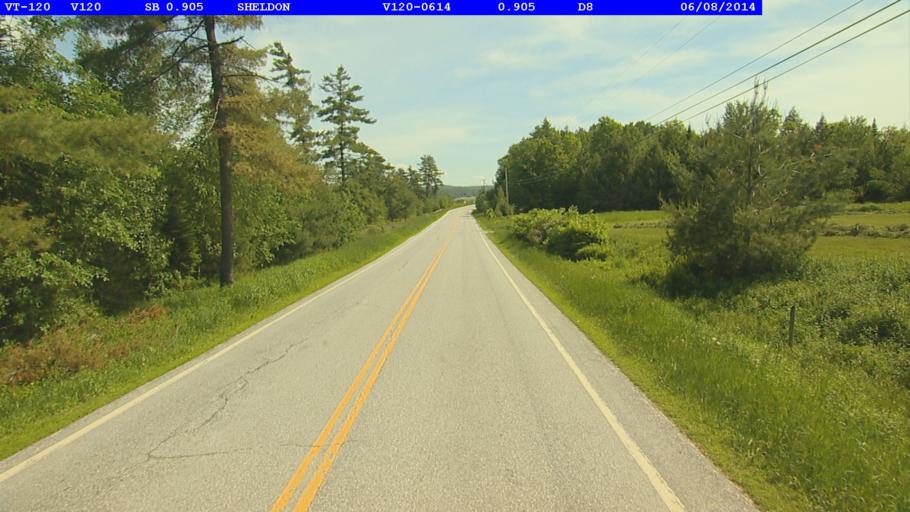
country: US
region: Vermont
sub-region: Franklin County
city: Enosburg Falls
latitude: 44.9231
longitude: -72.9017
